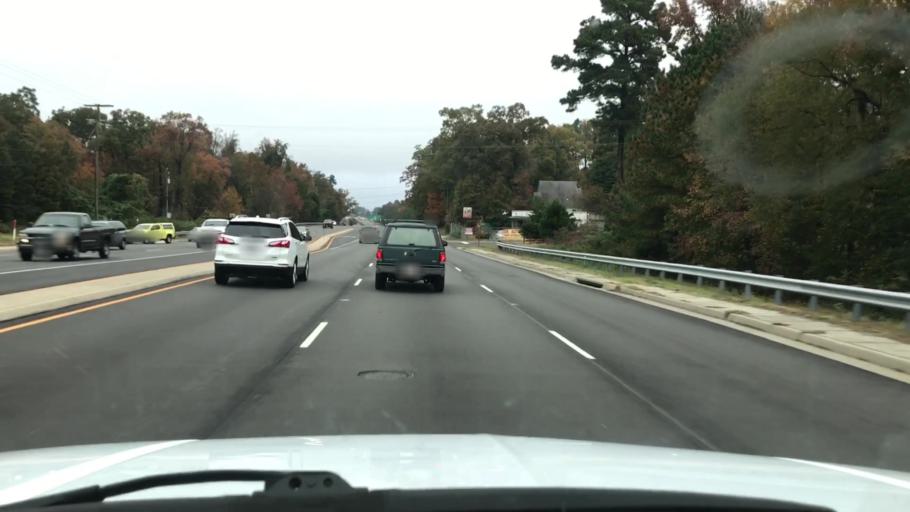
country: US
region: Virginia
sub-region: Henrico County
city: Chamberlayne
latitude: 37.6469
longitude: -77.4599
